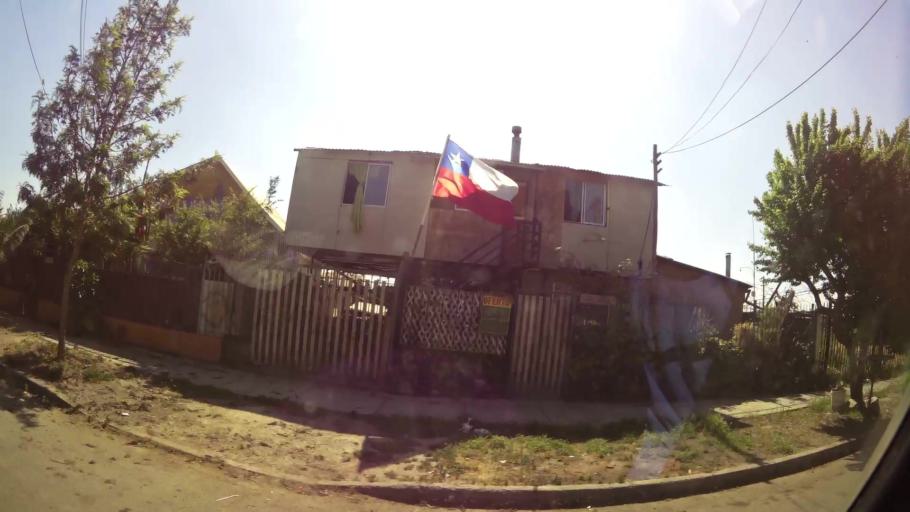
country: CL
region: Santiago Metropolitan
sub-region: Provincia de Talagante
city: Penaflor
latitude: -33.5685
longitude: -70.7994
